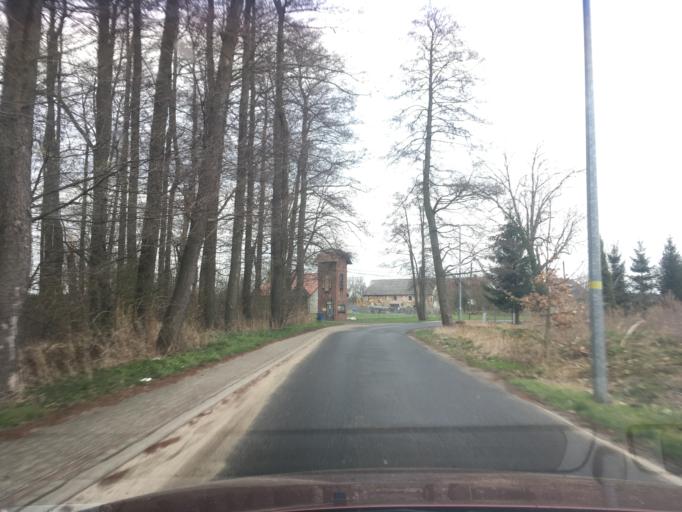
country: PL
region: Lower Silesian Voivodeship
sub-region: Powiat zgorzelecki
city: Lagow
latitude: 51.1490
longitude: 15.0443
